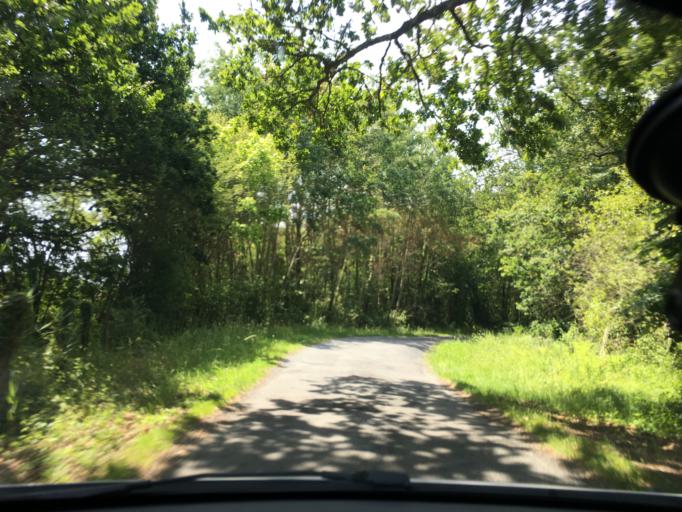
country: FR
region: Aquitaine
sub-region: Departement de la Gironde
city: Lesparre-Medoc
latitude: 45.2799
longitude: -0.9102
